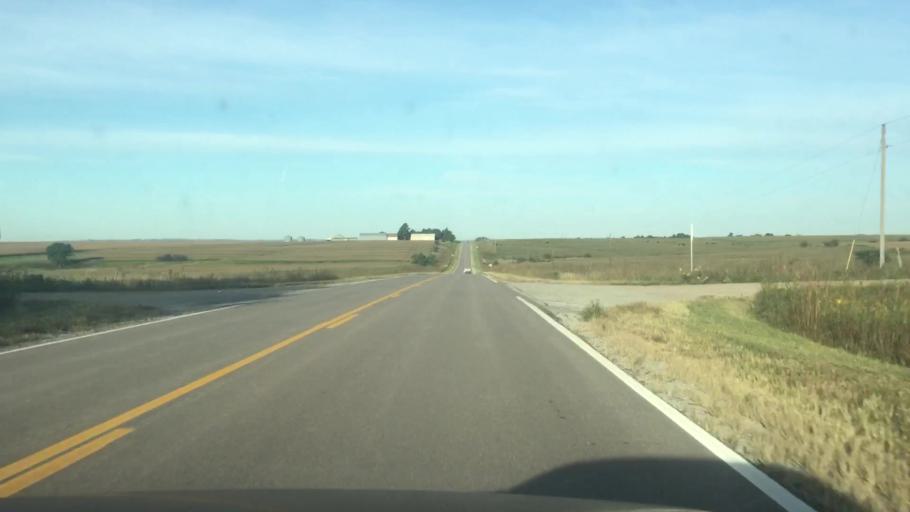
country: US
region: Nebraska
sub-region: Jefferson County
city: Fairbury
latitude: 40.0449
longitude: -96.9726
